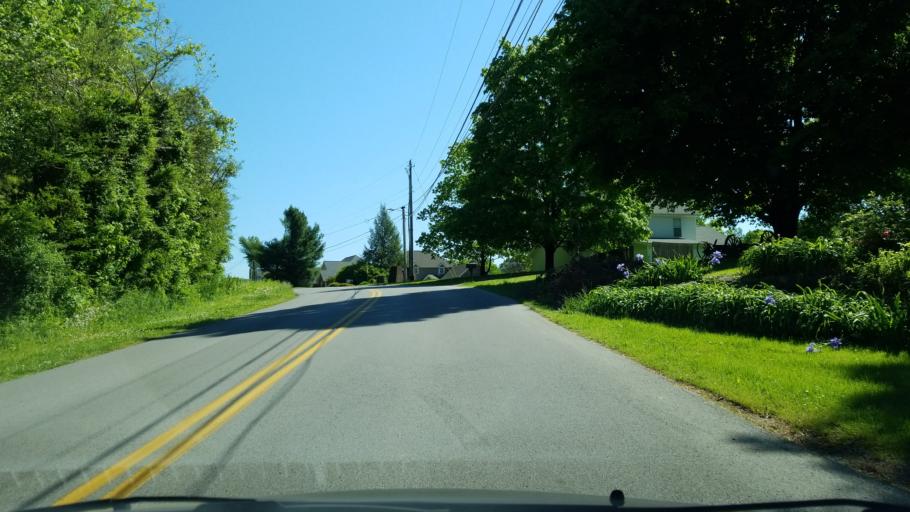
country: US
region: Tennessee
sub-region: Hamilton County
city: Red Bank
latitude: 35.1345
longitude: -85.3048
